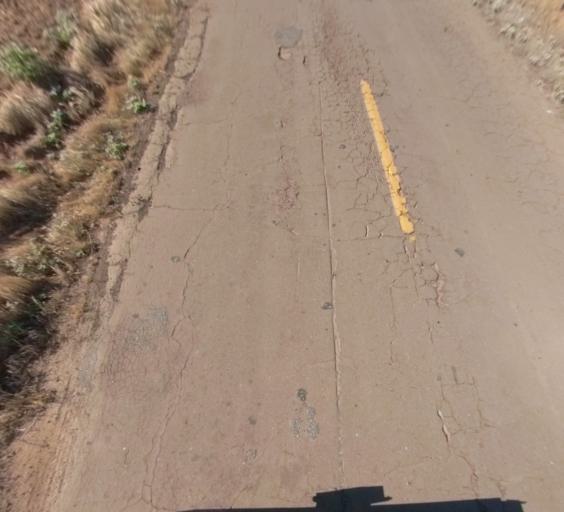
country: US
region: California
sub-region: Madera County
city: Bonadelle Ranchos-Madera Ranchos
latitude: 36.8830
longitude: -119.8111
